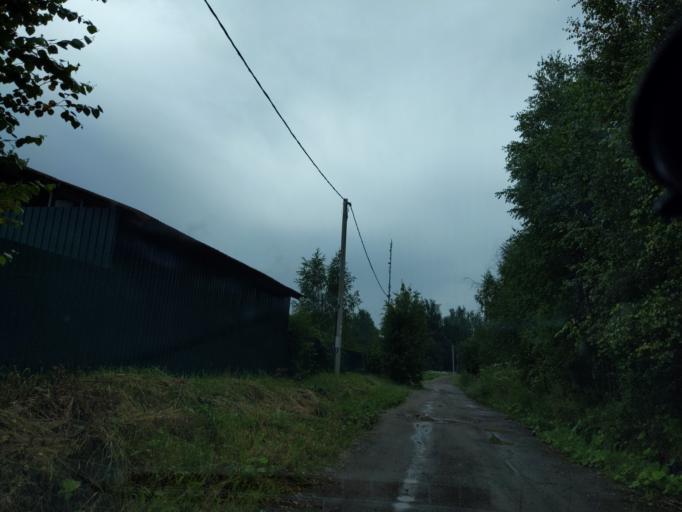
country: RU
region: Moskovskaya
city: Lugovaya
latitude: 56.0543
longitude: 37.4988
